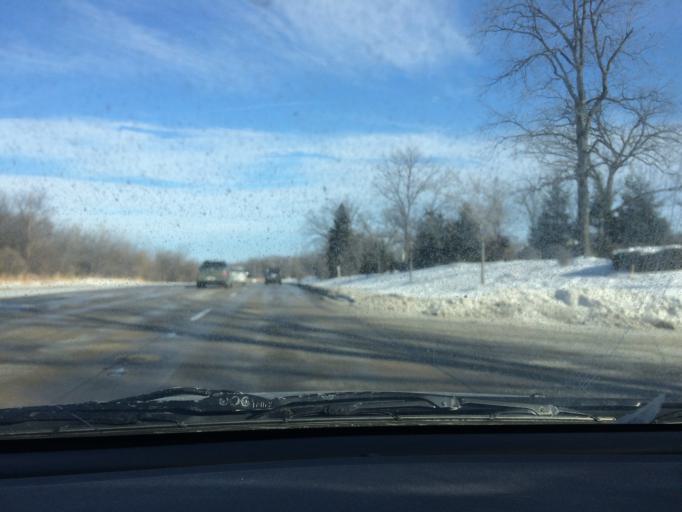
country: US
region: Illinois
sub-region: Cook County
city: Streamwood
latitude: 42.0392
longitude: -88.1962
